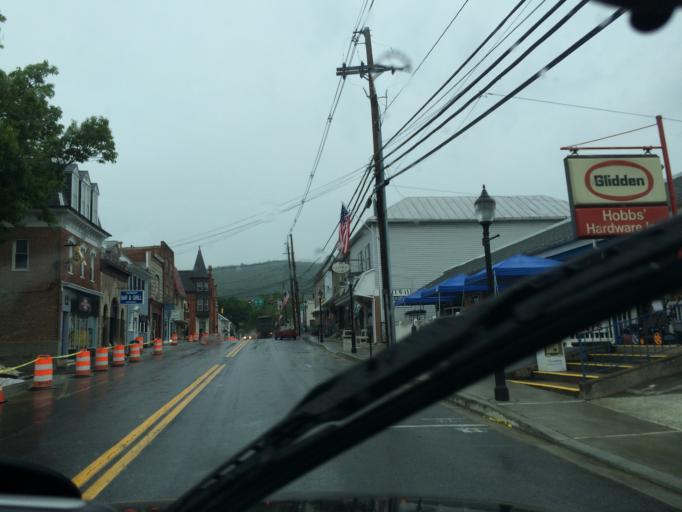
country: US
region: Maryland
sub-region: Frederick County
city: Thurmont
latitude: 39.6235
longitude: -77.4105
